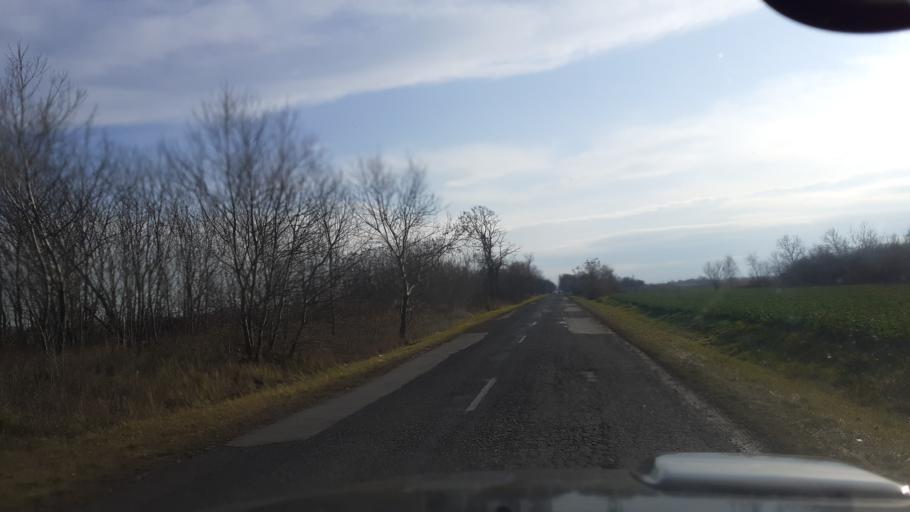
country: HU
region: Pest
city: Domsod
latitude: 47.1045
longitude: 19.0912
